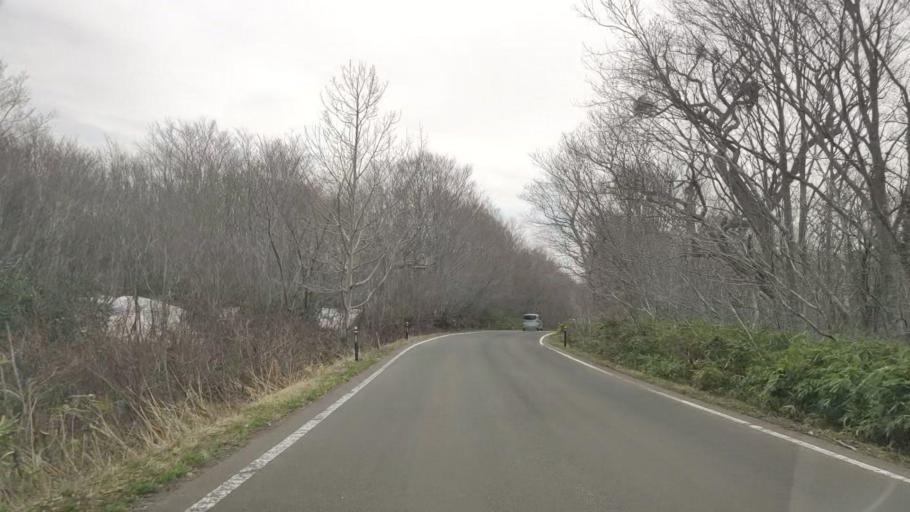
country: JP
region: Aomori
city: Aomori Shi
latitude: 40.6657
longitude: 140.9562
